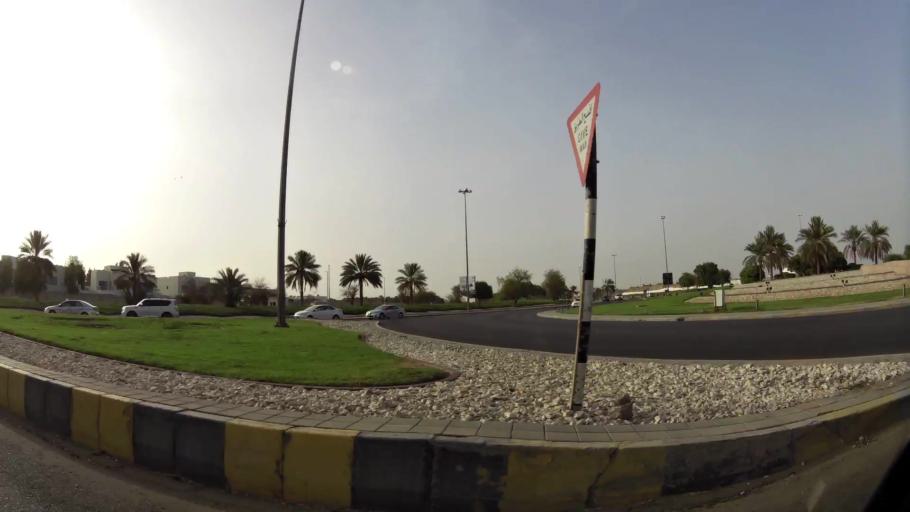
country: AE
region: Abu Dhabi
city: Al Ain
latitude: 24.2303
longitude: 55.7191
